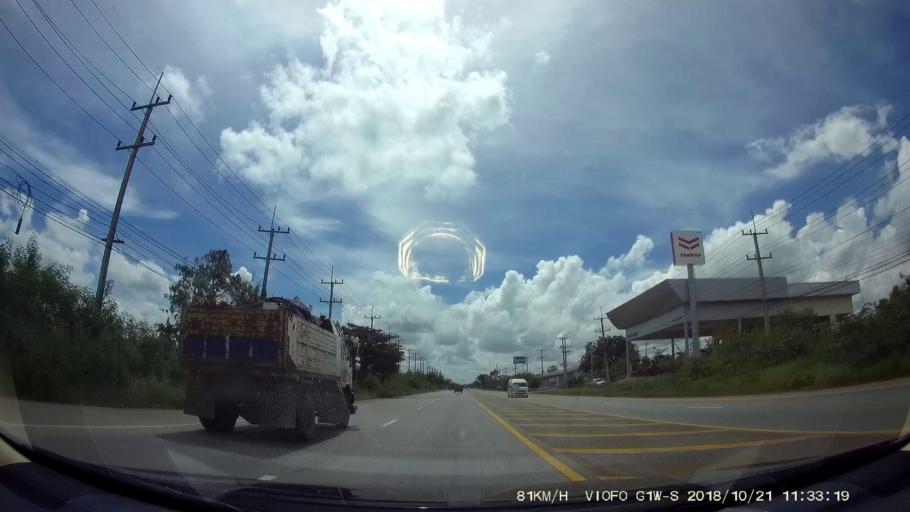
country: TH
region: Chaiyaphum
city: Chaiyaphum
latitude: 15.7472
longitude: 102.0242
